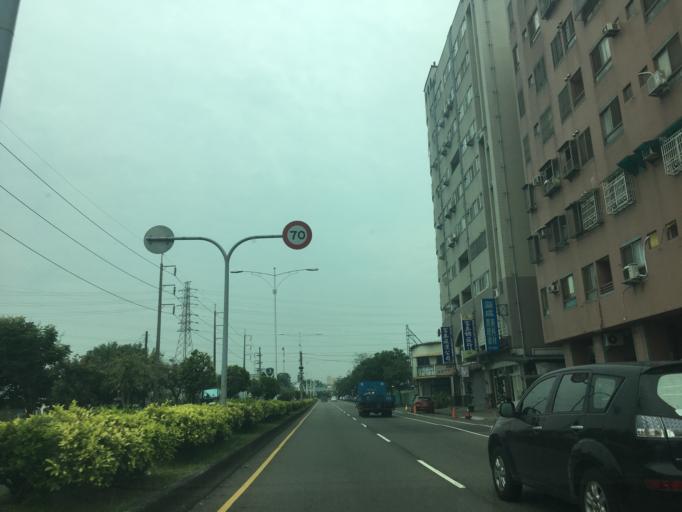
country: TW
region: Taiwan
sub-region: Taichung City
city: Taichung
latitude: 24.0709
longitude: 120.6975
